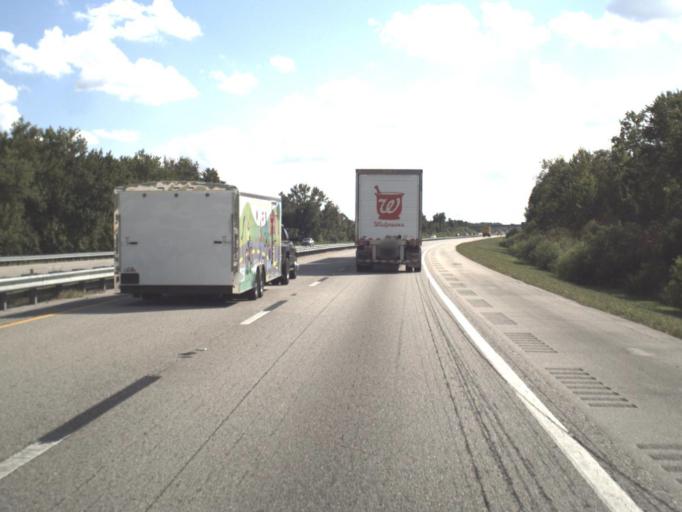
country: US
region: Florida
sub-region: Indian River County
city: Fellsmere
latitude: 27.7080
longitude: -80.8956
